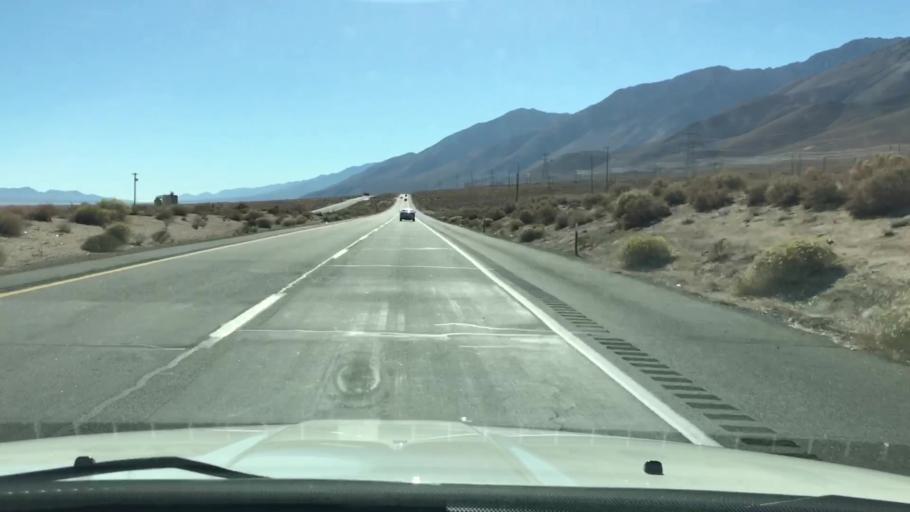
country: US
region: California
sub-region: Inyo County
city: Lone Pine
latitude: 36.4895
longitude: -118.0343
